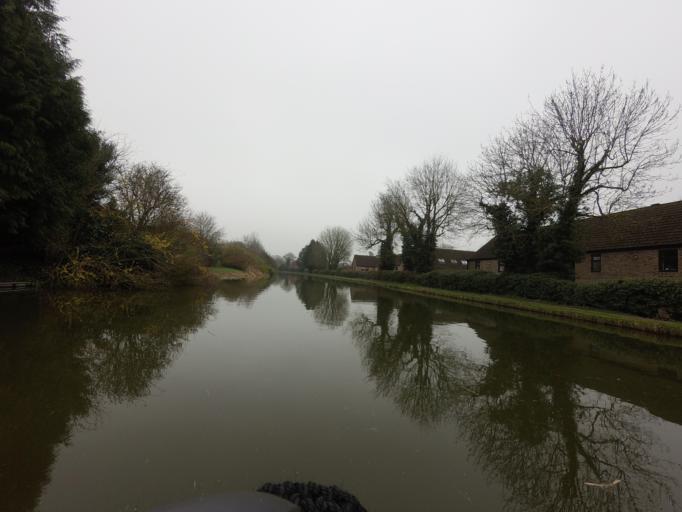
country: GB
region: England
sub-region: Hertfordshire
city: Berkhamsted
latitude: 51.7697
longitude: -0.5872
